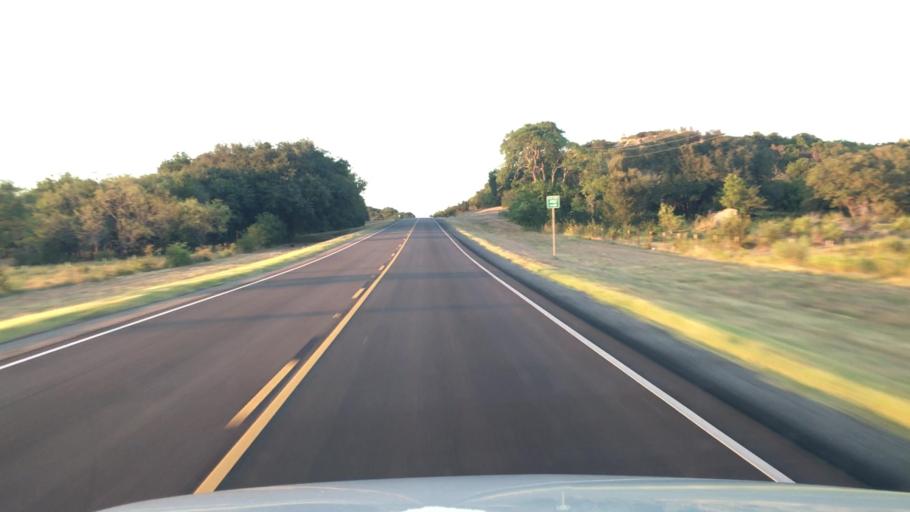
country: US
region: Texas
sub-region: Hamilton County
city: Hico
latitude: 32.0942
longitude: -97.9687
